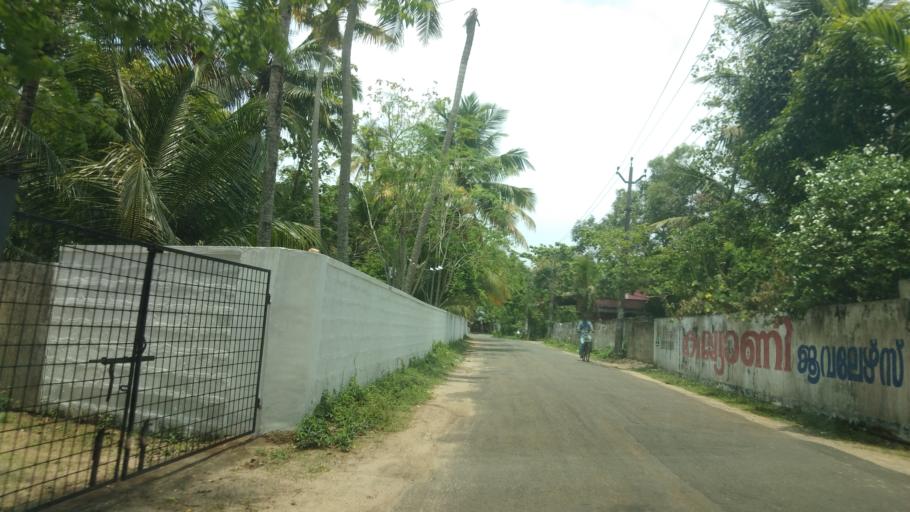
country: IN
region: Kerala
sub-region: Alappuzha
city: Vayalar
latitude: 9.6660
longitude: 76.3129
